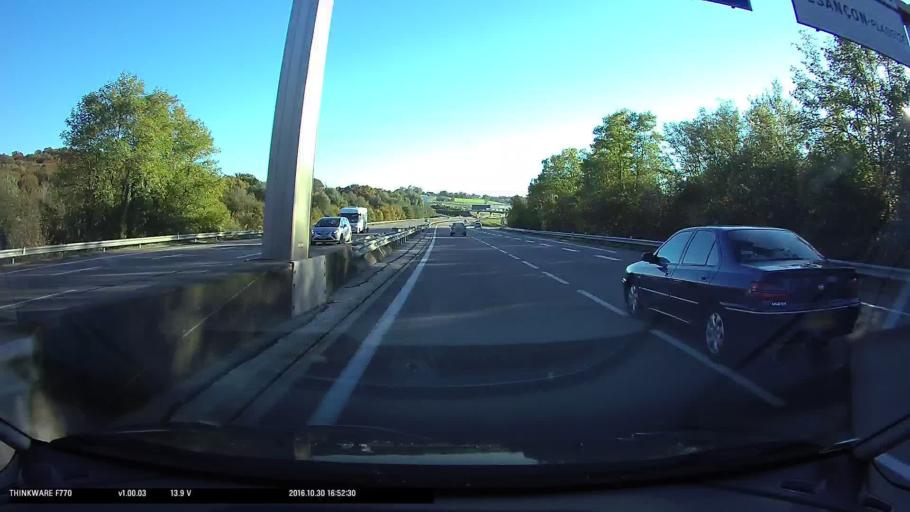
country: FR
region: Franche-Comte
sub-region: Departement du Doubs
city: Chemaudin
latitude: 47.2402
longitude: 5.8943
